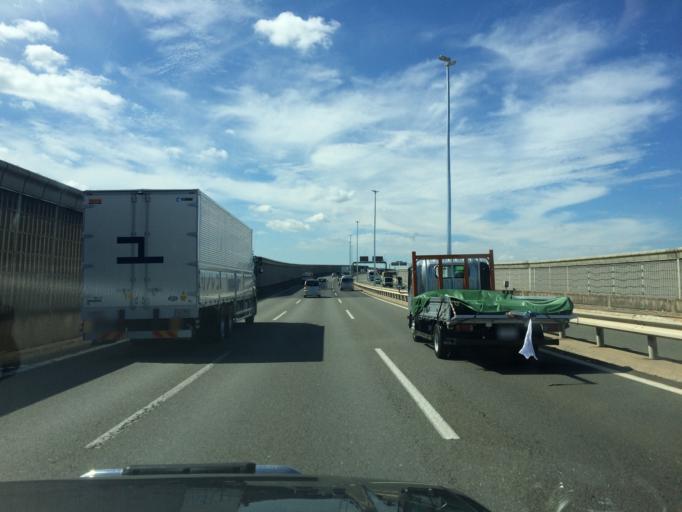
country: JP
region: Osaka
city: Matsubara
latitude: 34.5474
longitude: 135.5609
